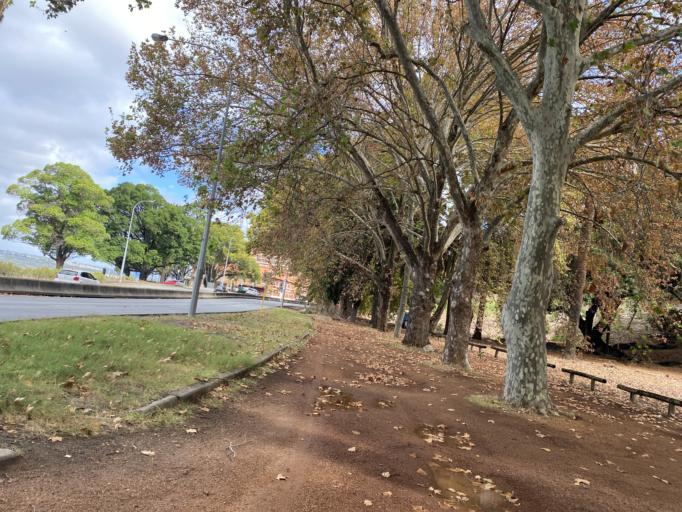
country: AU
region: Western Australia
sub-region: City of Perth
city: West Perth
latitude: -31.9632
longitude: 115.8421
